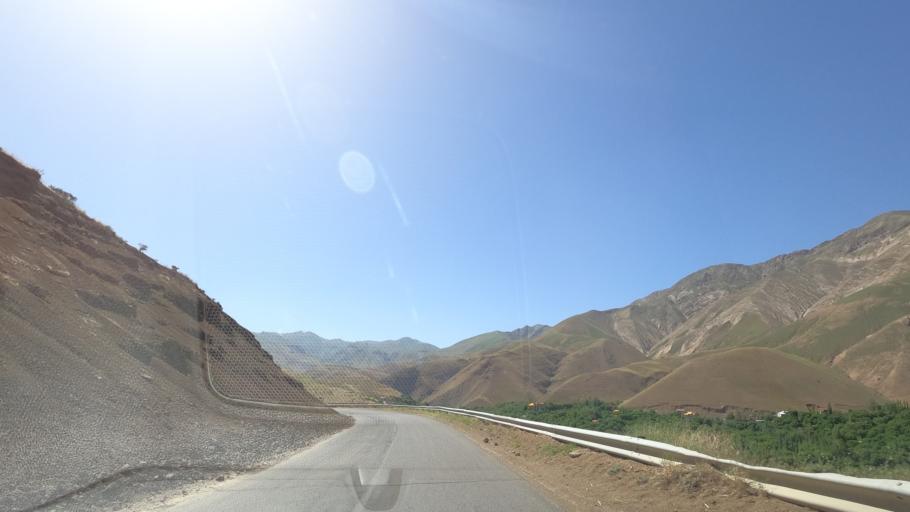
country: IR
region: Alborz
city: Karaj
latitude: 35.9264
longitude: 51.0875
